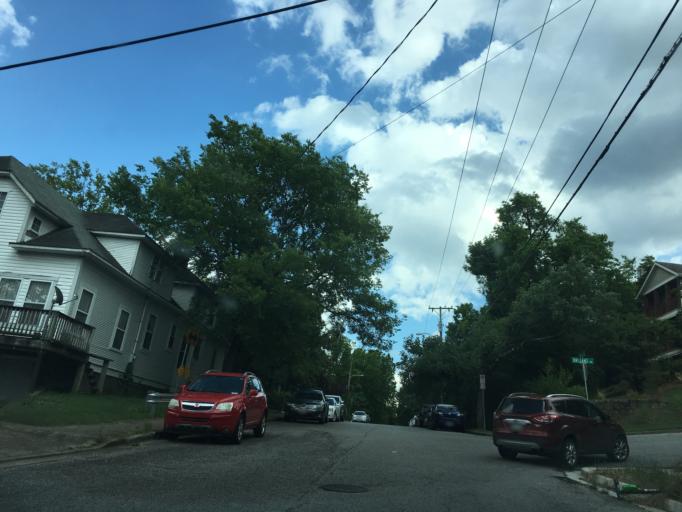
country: US
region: Tennessee
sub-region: Davidson County
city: Nashville
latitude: 36.1405
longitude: -86.8151
